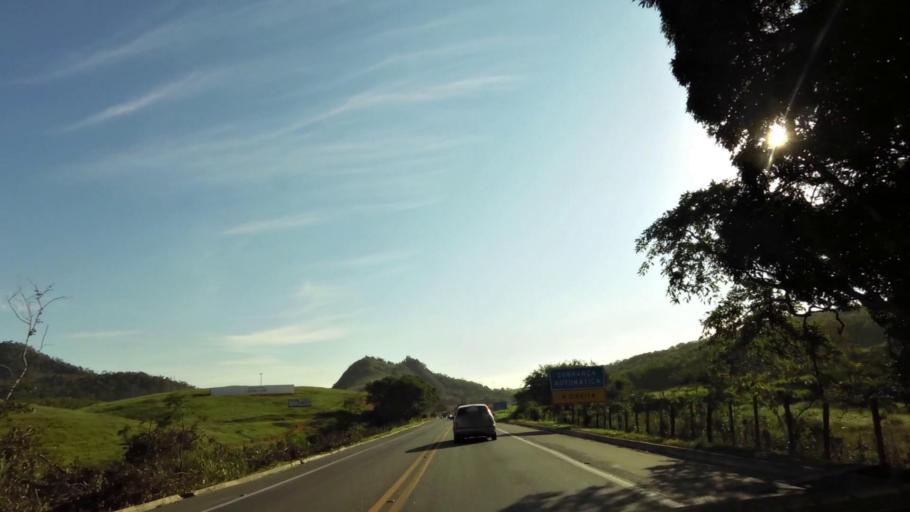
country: BR
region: Espirito Santo
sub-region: Guarapari
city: Guarapari
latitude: -20.5254
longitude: -40.4805
